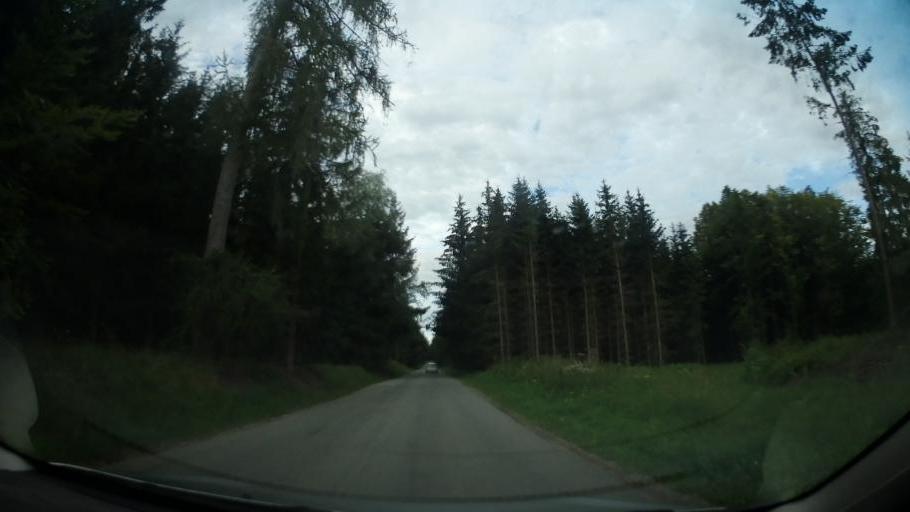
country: CZ
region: Olomoucky
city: Horni Stepanov
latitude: 49.5377
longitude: 16.7260
